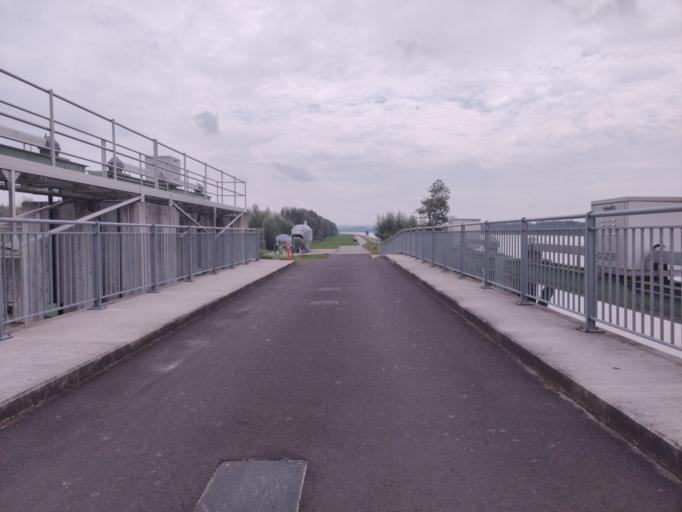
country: AT
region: Upper Austria
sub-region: Politischer Bezirk Perg
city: Perg
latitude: 48.2196
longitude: 14.5923
